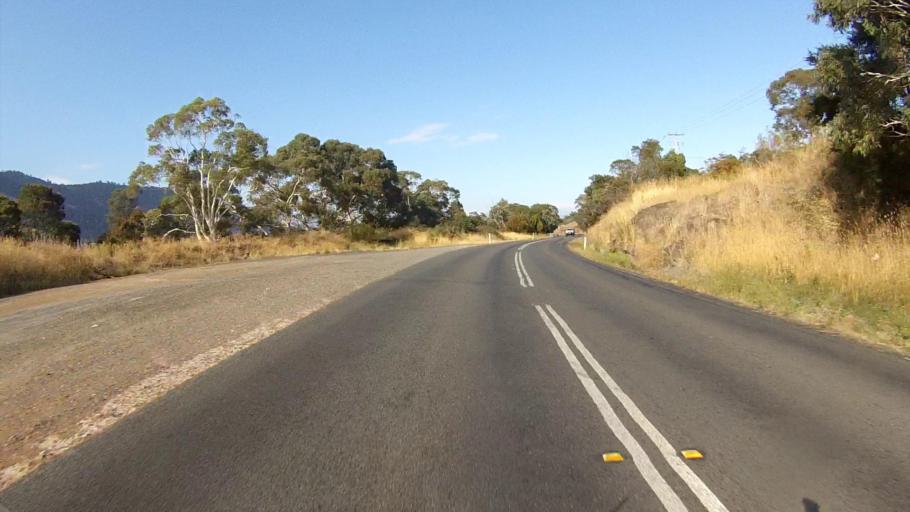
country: AU
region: Tasmania
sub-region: Glenorchy
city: Granton
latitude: -42.7565
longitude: 147.1424
